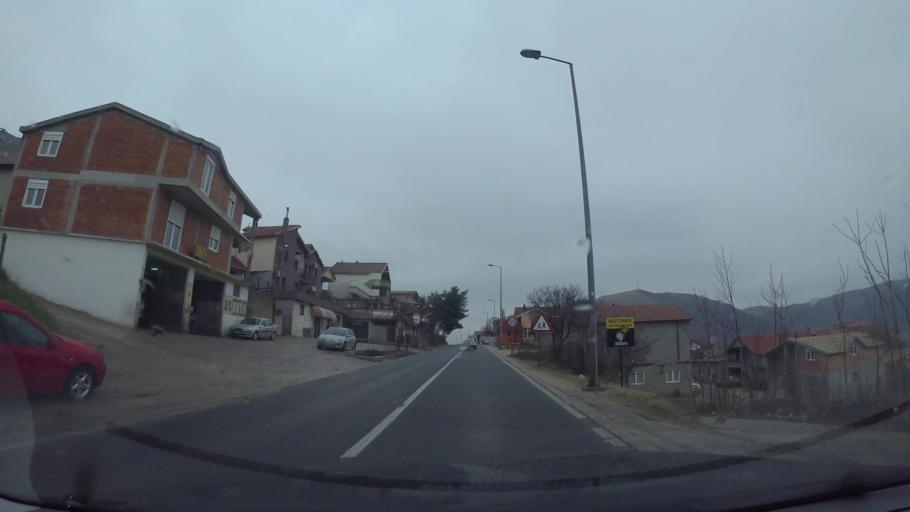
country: BA
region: Federation of Bosnia and Herzegovina
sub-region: Hercegovacko-Bosanski Kanton
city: Mostar
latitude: 43.3478
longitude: 17.8168
